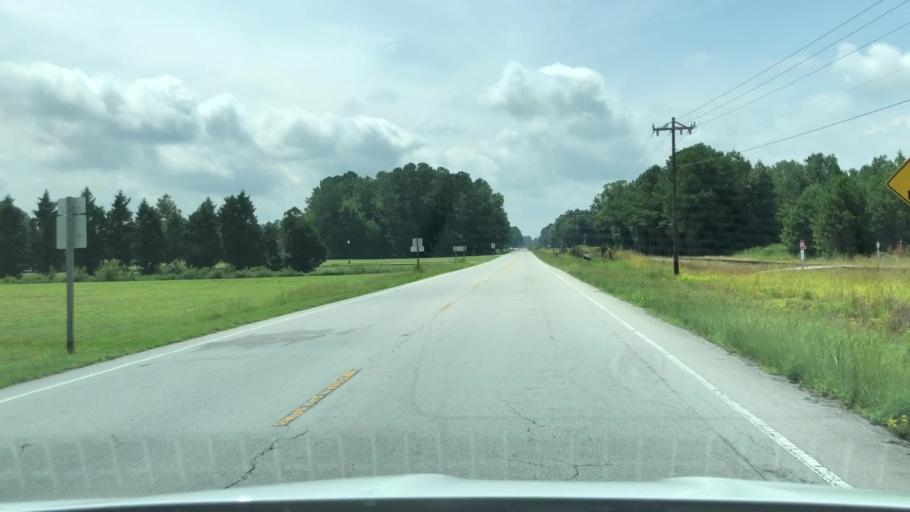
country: US
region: North Carolina
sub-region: Craven County
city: Vanceboro
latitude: 35.3423
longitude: -77.1510
